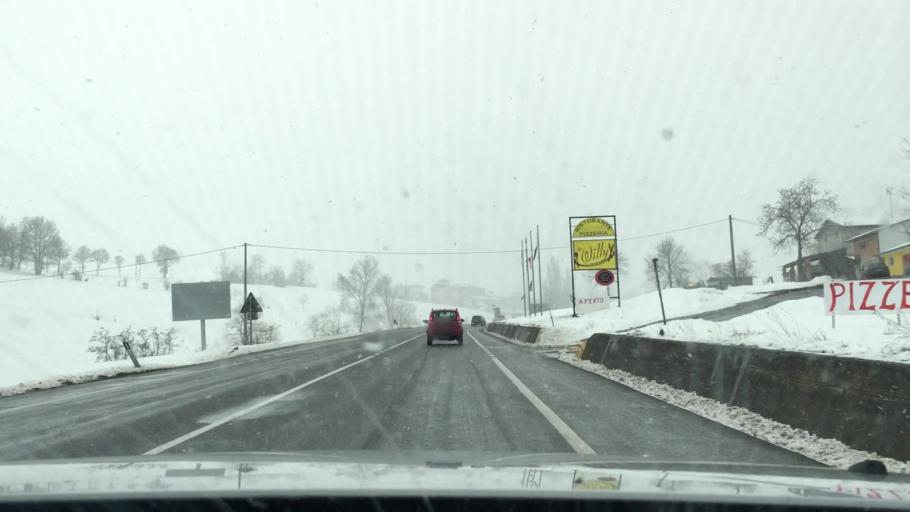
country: IT
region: Emilia-Romagna
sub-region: Provincia di Modena
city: Sant'Antonio
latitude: 44.4120
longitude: 10.8455
